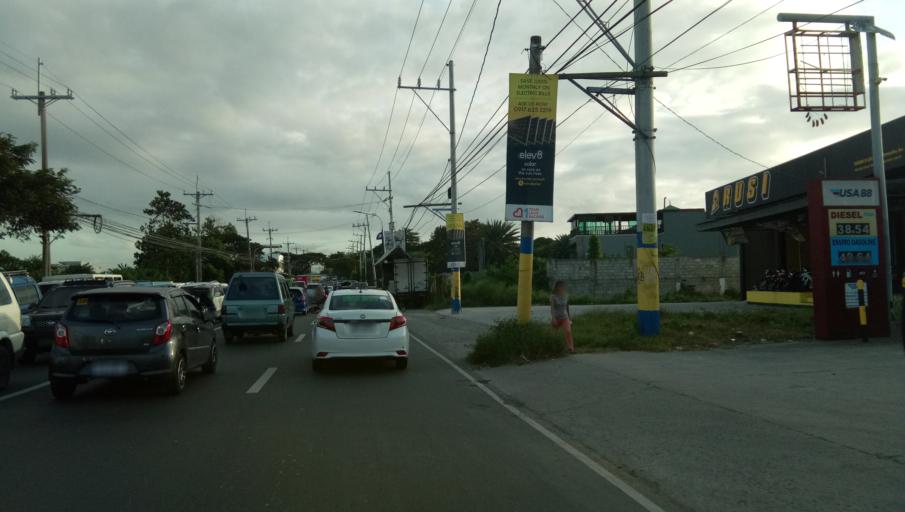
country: PH
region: Calabarzon
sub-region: Province of Cavite
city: Dasmarinas
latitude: 14.3793
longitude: 120.9789
